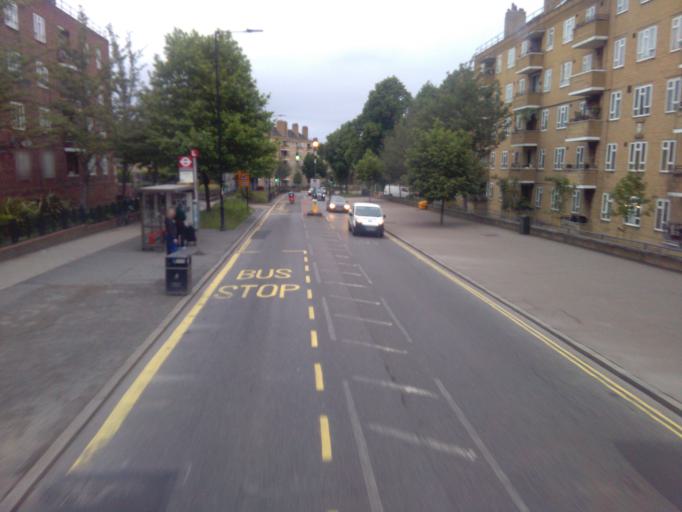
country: GB
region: England
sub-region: Greater London
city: Brixton Hill
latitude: 51.4514
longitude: -0.1133
